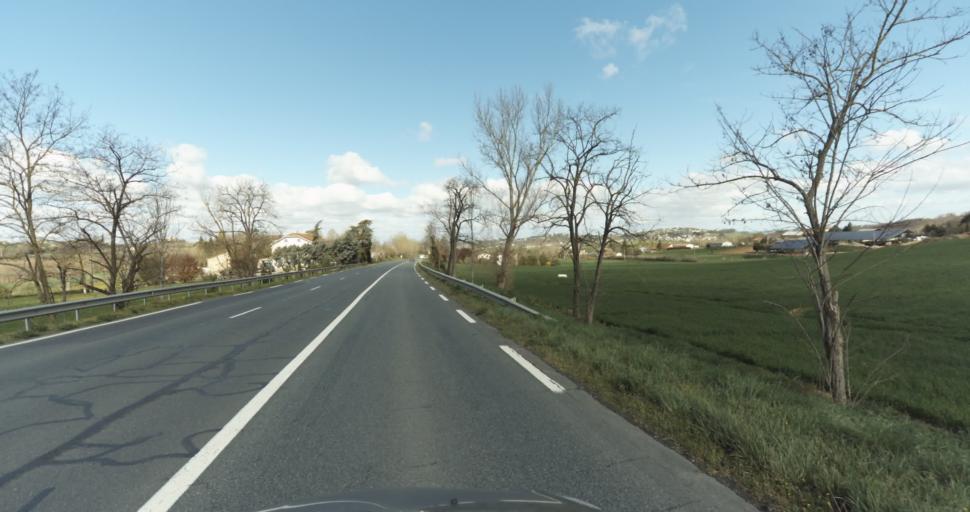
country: FR
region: Midi-Pyrenees
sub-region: Departement du Tarn
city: Puygouzon
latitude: 43.8714
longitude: 2.1819
